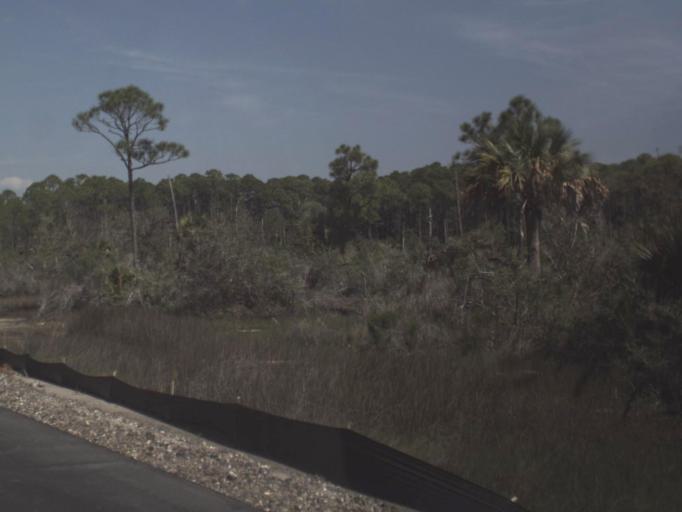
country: US
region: Florida
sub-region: Gulf County
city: Port Saint Joe
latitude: 29.6873
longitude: -85.3090
